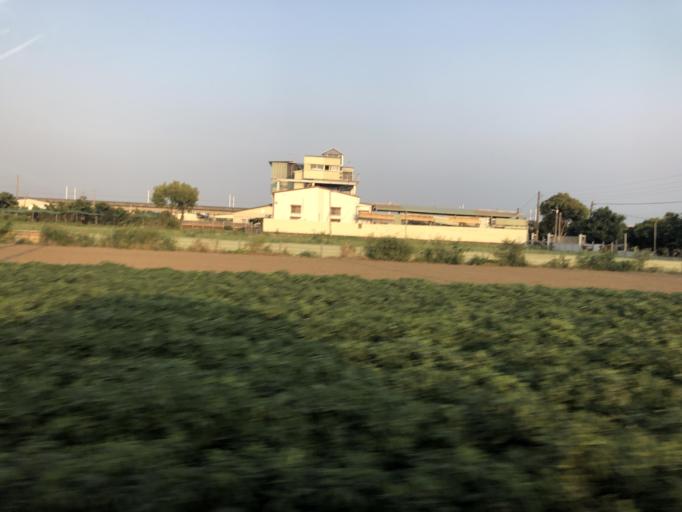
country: TW
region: Taiwan
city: Xinying
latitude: 23.1482
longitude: 120.2732
